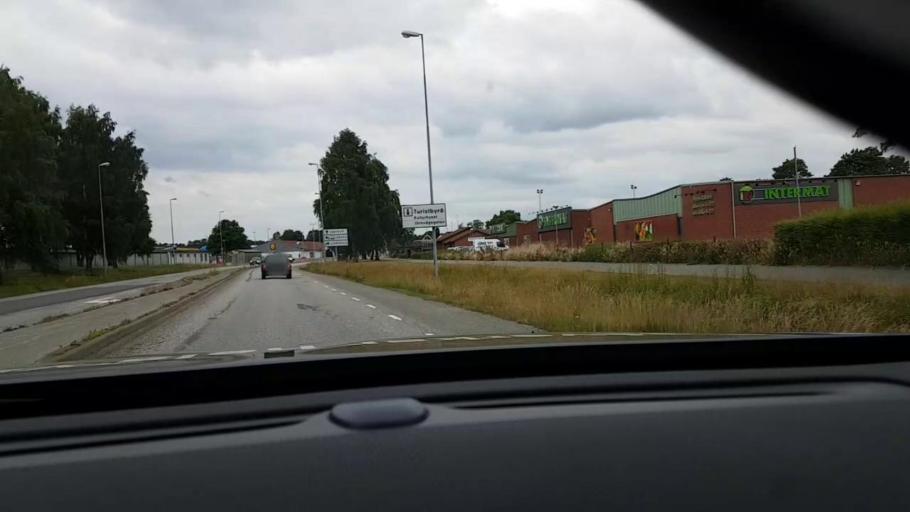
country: SE
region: Skane
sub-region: Hassleholms Kommun
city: Hassleholm
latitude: 56.1673
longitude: 13.7899
